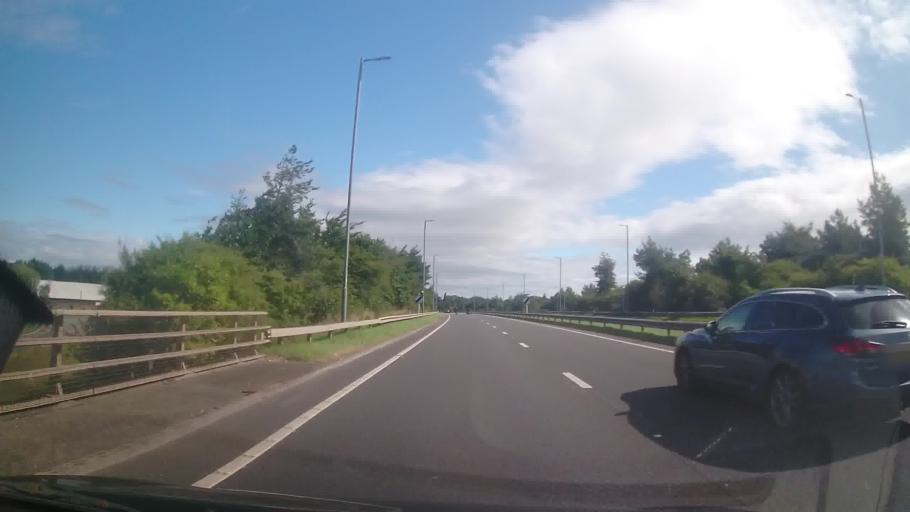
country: GB
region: Wales
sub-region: Wrexham
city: Gresford
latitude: 53.0725
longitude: -2.9903
